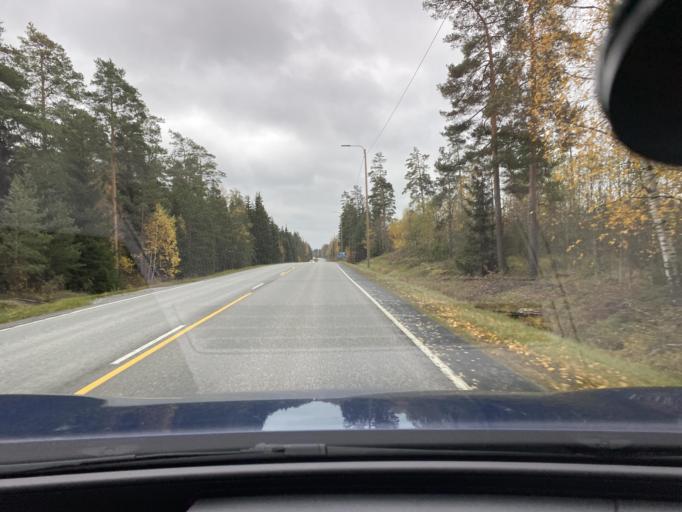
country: FI
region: Varsinais-Suomi
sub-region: Vakka-Suomi
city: Laitila
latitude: 60.9673
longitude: 21.5941
